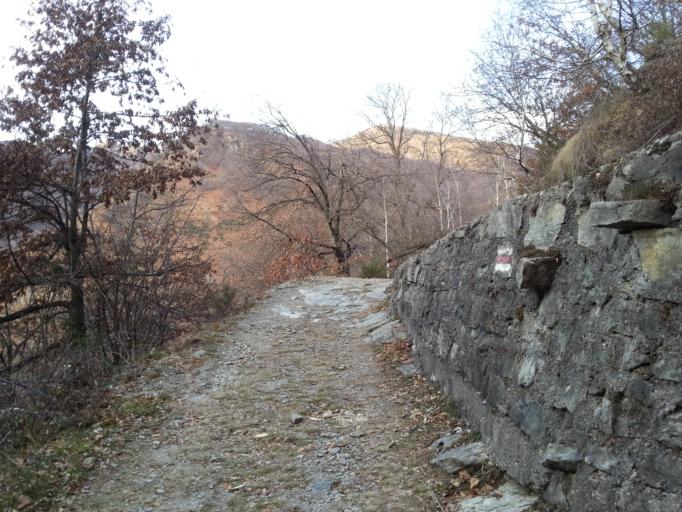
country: CH
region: Ticino
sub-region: Lugano District
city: Gravesano
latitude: 46.0557
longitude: 8.8875
